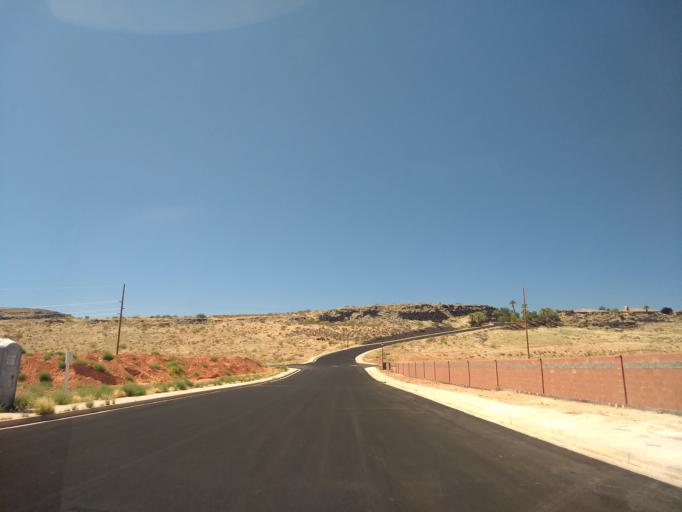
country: US
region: Utah
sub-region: Washington County
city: Washington
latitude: 37.1288
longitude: -113.4976
